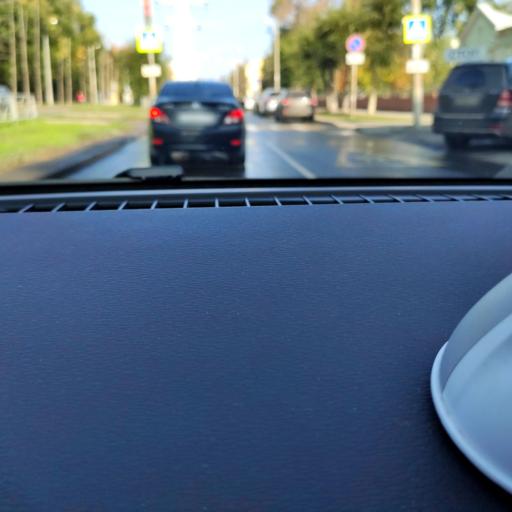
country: RU
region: Samara
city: Samara
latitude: 53.1990
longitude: 50.2141
